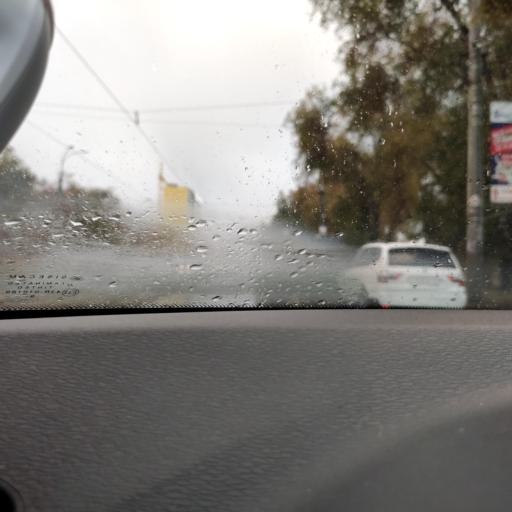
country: RU
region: Samara
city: Smyshlyayevka
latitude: 53.2045
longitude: 50.2803
